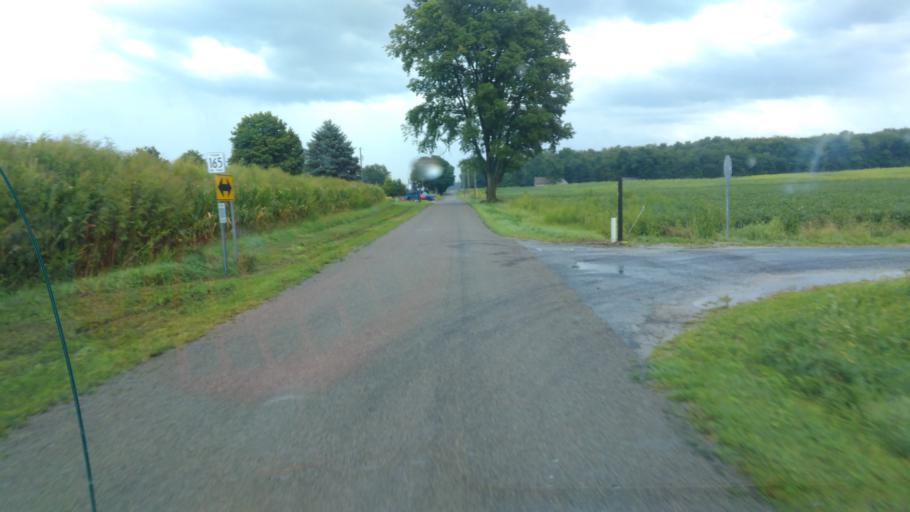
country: US
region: Ohio
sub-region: Hardin County
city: Kenton
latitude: 40.6890
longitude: -83.6095
